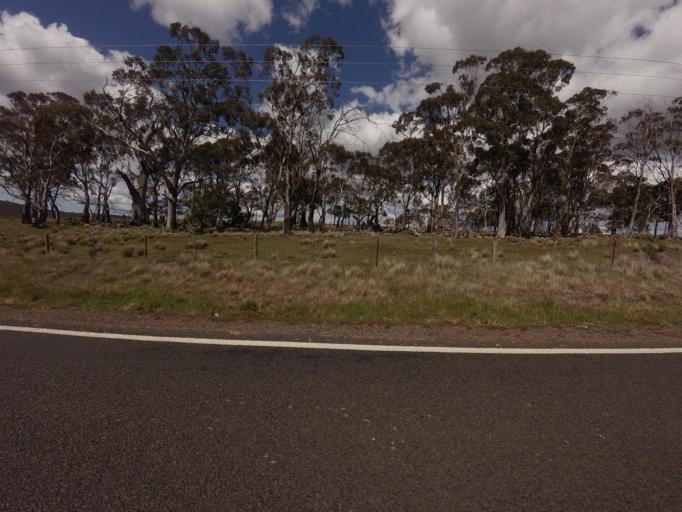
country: AU
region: Tasmania
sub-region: Northern Midlands
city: Evandale
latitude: -41.9438
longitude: 147.6042
